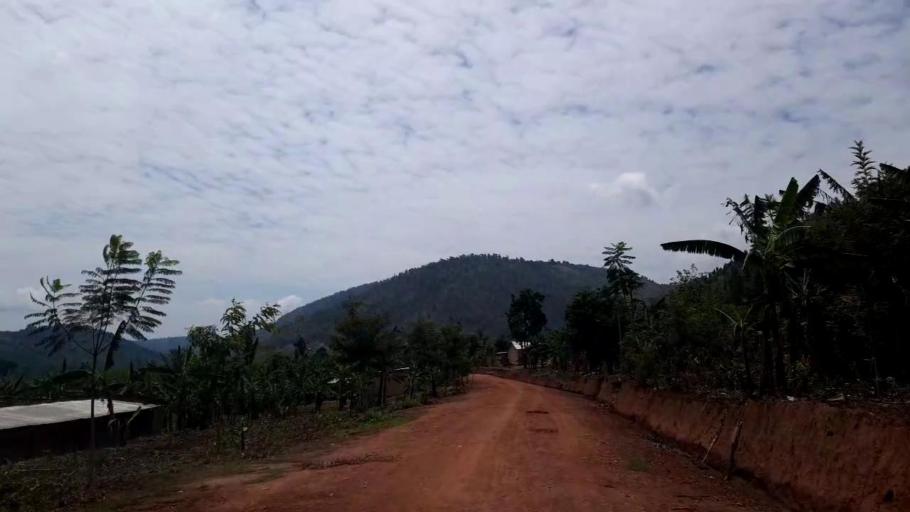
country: RW
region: Northern Province
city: Byumba
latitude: -1.5035
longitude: 30.1934
